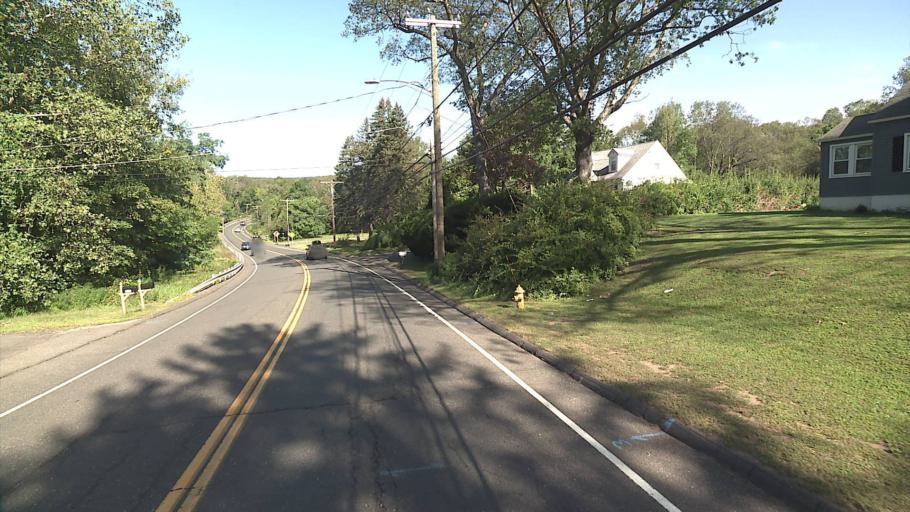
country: US
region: Connecticut
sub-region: New Haven County
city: Cheshire Village
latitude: 41.5172
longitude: -72.9277
